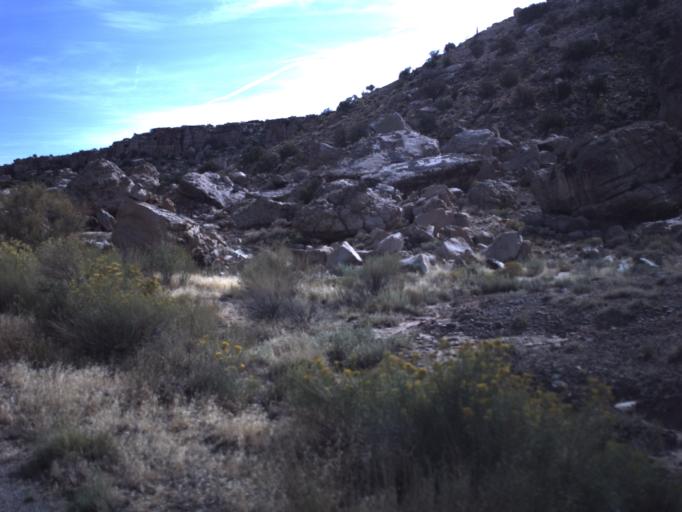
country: US
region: Utah
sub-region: San Juan County
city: Blanding
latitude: 37.4291
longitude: -109.4096
